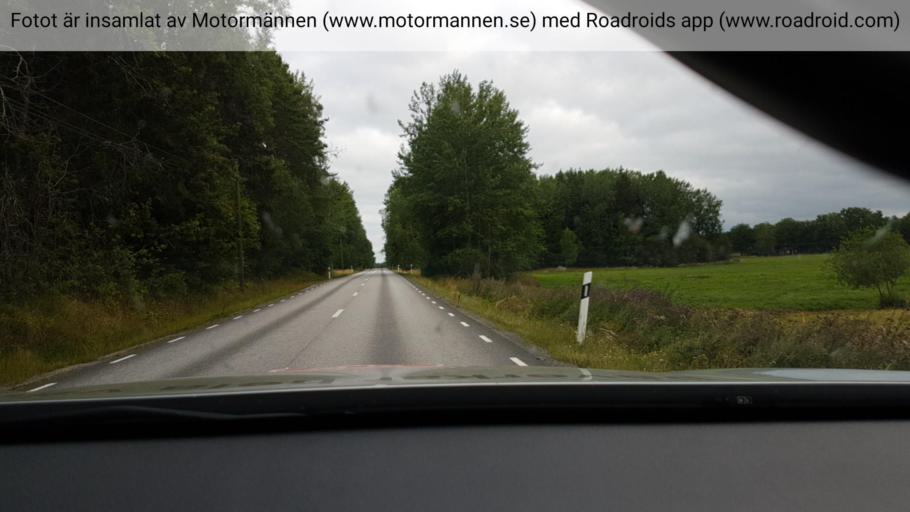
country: SE
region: Stockholm
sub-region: Norrtalje Kommun
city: Skanninge
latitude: 59.8328
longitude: 18.4423
